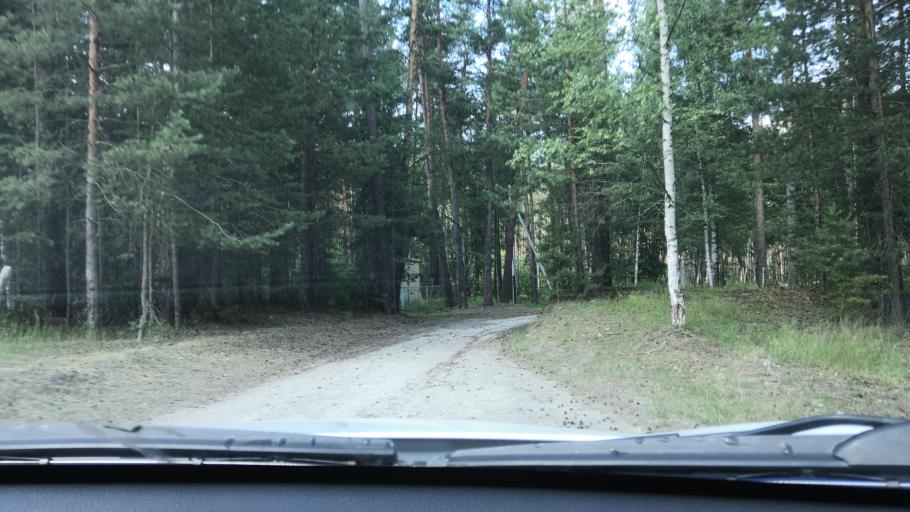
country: RU
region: Rjazan
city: Murmino
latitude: 54.5378
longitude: 40.1721
